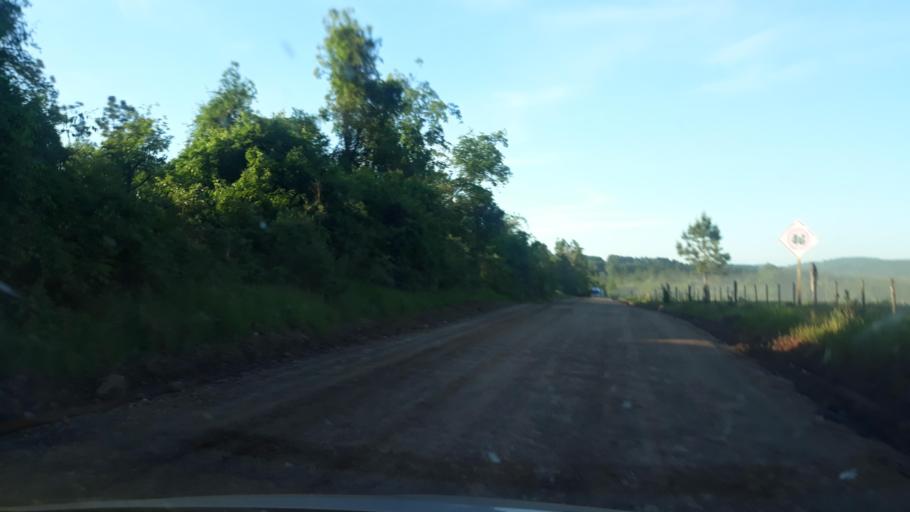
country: AR
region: Misiones
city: Ruiz de Montoya
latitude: -27.0489
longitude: -55.0040
